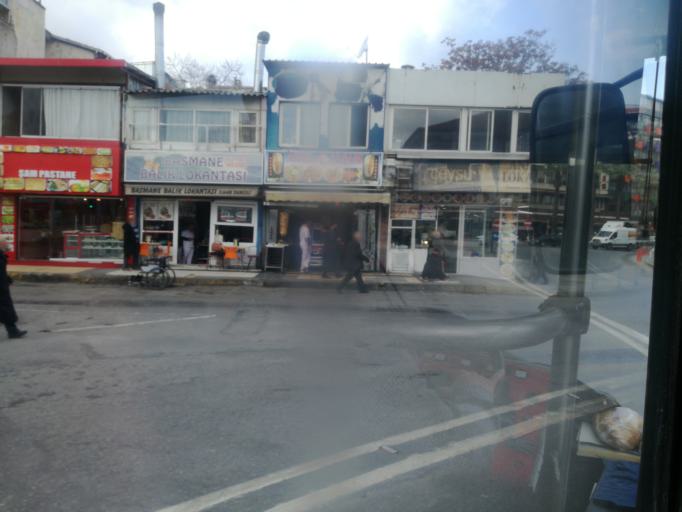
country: TR
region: Izmir
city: Izmir
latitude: 38.4221
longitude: 27.1436
